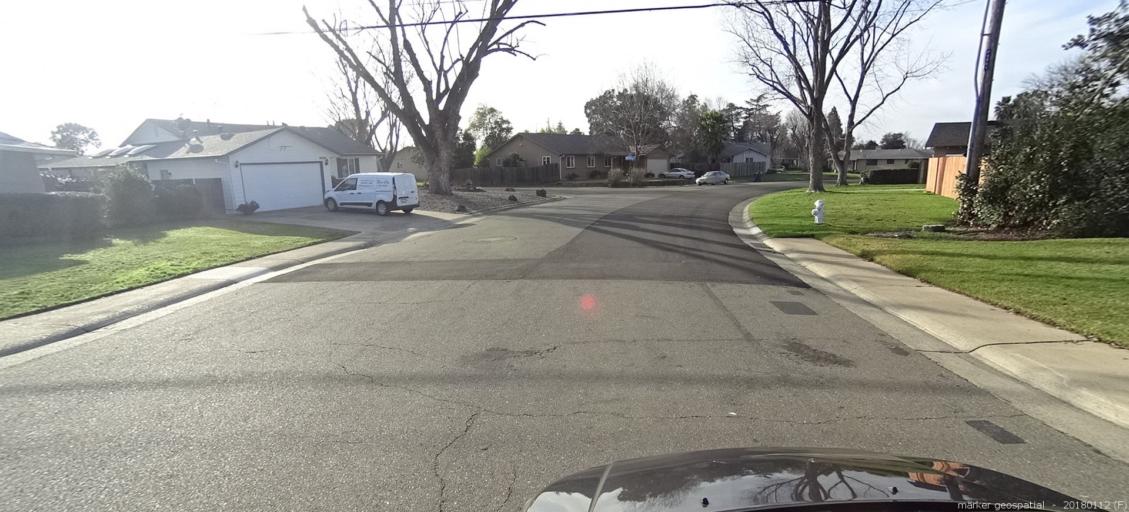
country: US
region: California
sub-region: Sacramento County
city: Rancho Cordova
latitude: 38.6011
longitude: -121.2891
